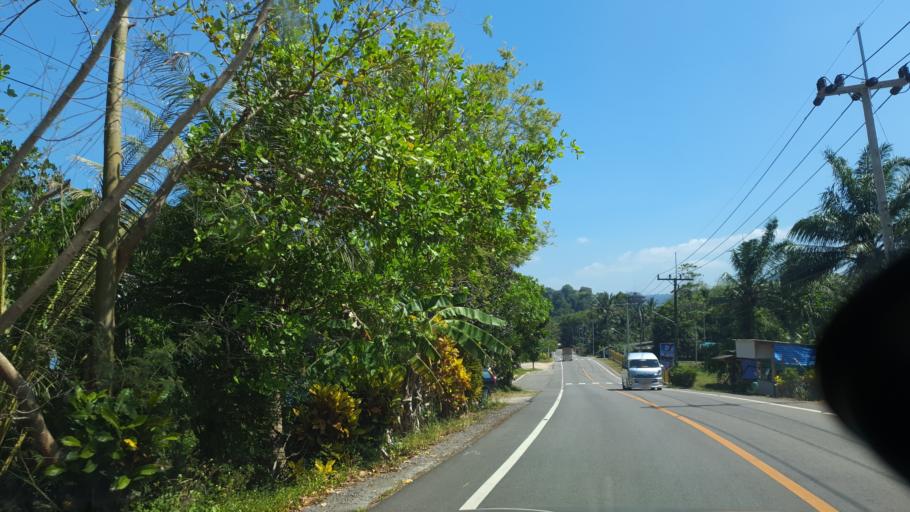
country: TH
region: Krabi
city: Khlong Thom
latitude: 7.9284
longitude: 99.2358
